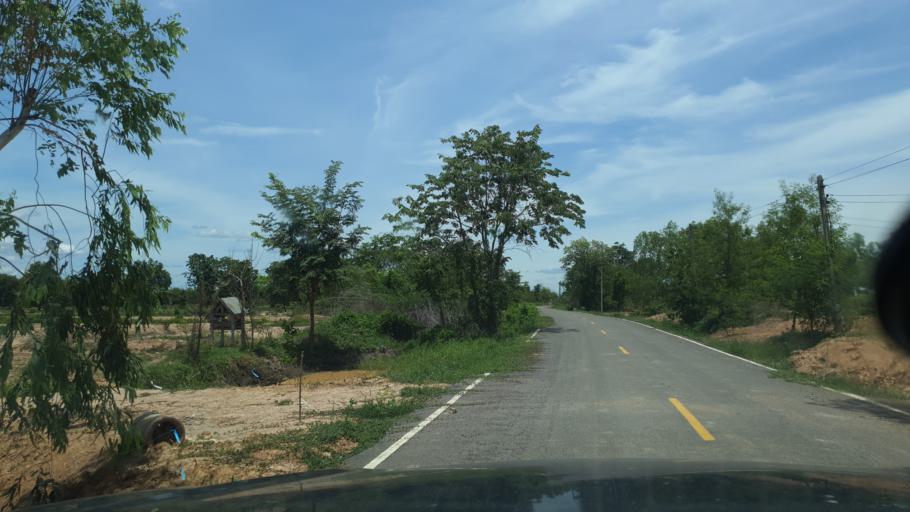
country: TH
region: Sukhothai
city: Ban Na
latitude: 17.1505
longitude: 99.6626
